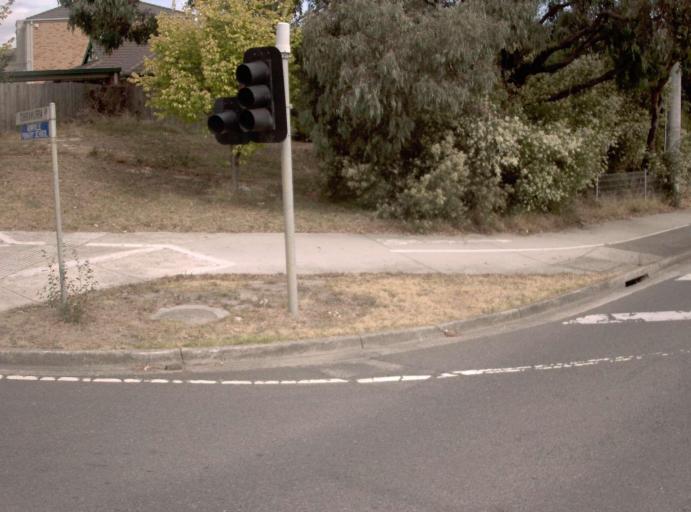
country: AU
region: Victoria
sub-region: Knox
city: Rowville
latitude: -37.9228
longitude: 145.2342
